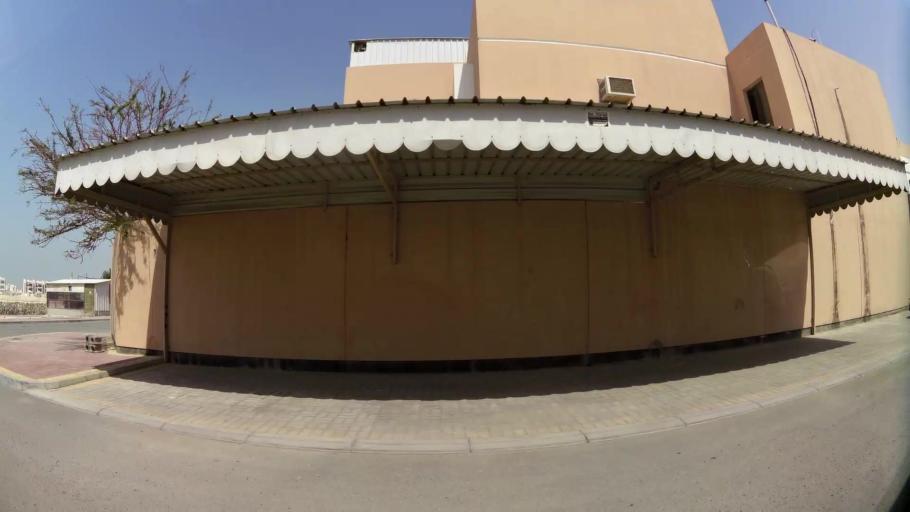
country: BH
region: Manama
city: Jidd Hafs
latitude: 26.2175
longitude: 50.4464
